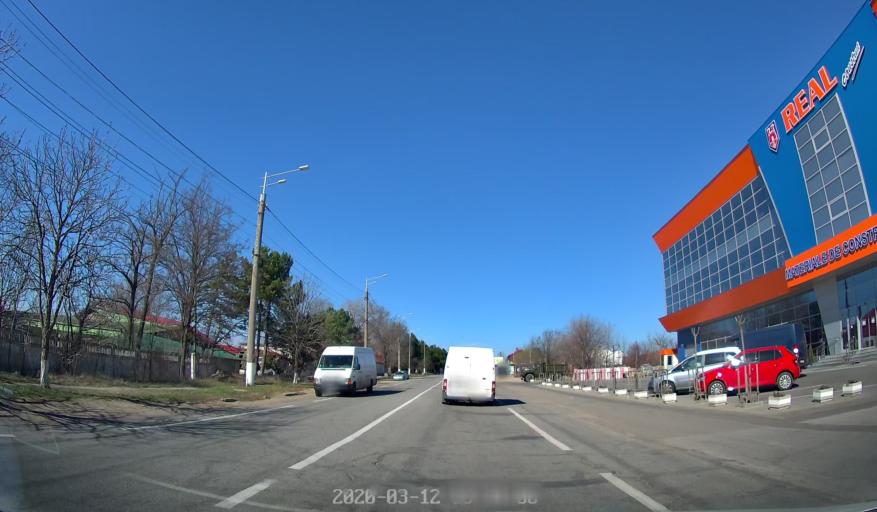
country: MD
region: Laloveni
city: Ialoveni
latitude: 46.9611
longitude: 28.7677
